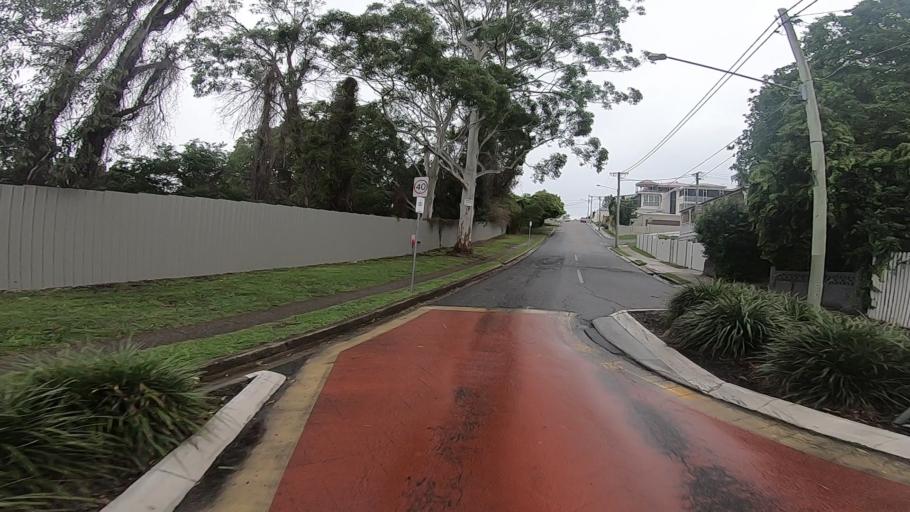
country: AU
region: Queensland
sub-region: Brisbane
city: Ascot
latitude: -27.4372
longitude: 153.0491
